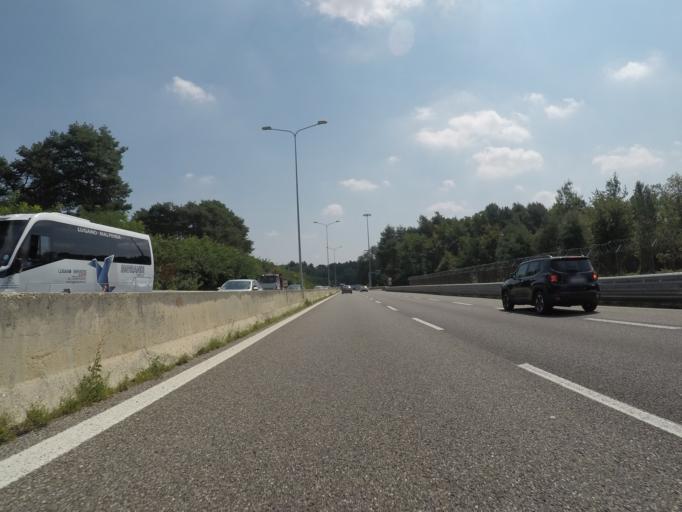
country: IT
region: Lombardy
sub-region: Provincia di Varese
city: Casorate Sempione
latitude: 45.6541
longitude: 8.7399
